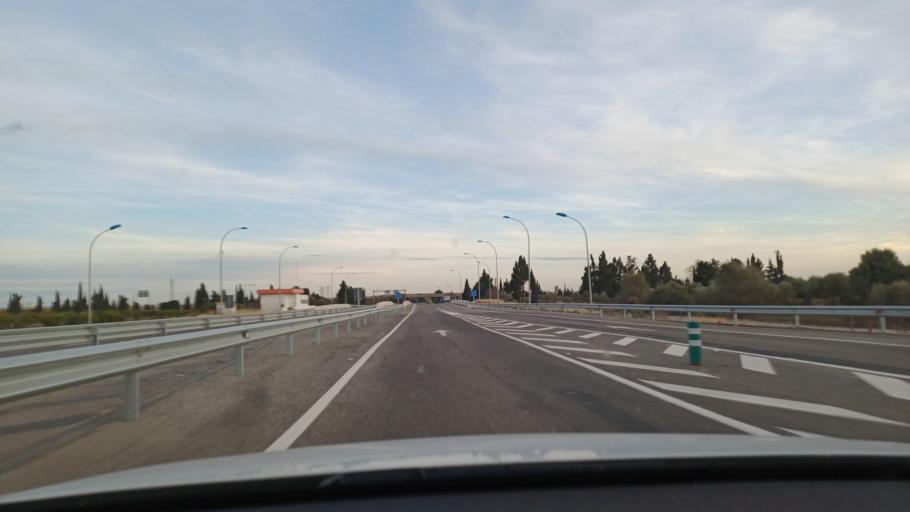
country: ES
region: Catalonia
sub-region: Provincia de Tarragona
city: Amposta
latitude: 40.7286
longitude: 0.5868
